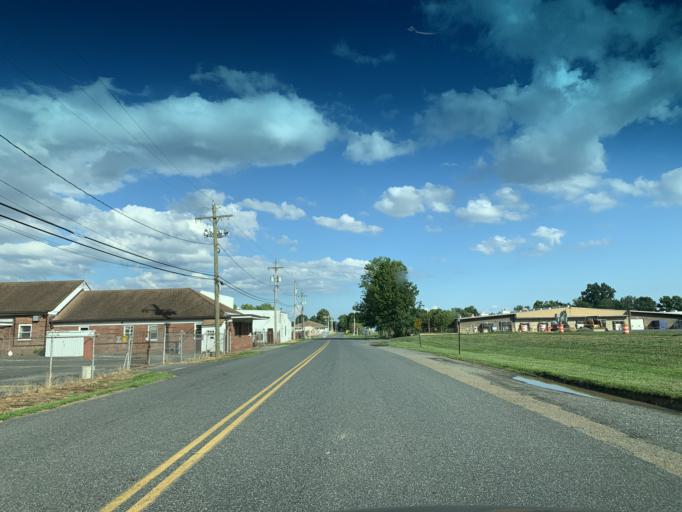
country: US
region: Maryland
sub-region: Harford County
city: Havre de Grace
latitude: 39.5334
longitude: -76.1075
